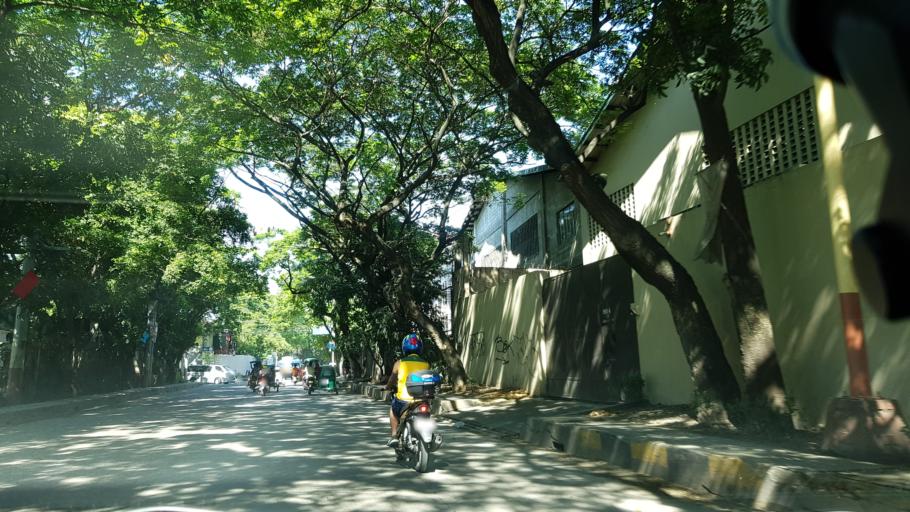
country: PH
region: Calabarzon
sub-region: Province of Rizal
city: Cainta
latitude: 14.5710
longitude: 121.0924
